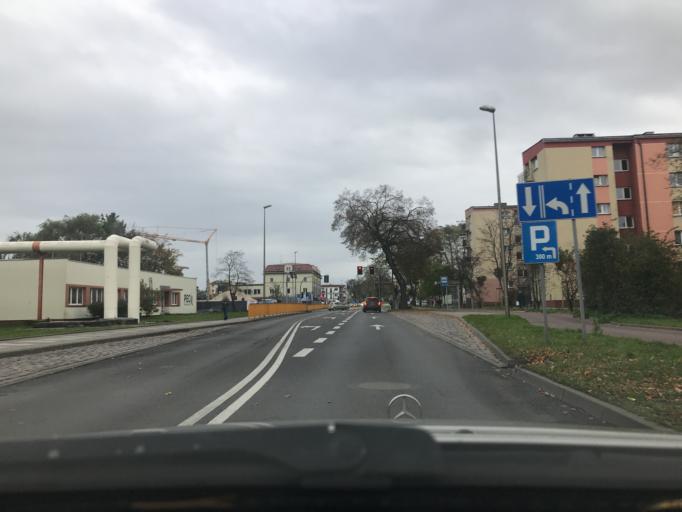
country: PL
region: West Pomeranian Voivodeship
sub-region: Swinoujscie
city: Swinoujscie
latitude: 53.9064
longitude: 14.2446
